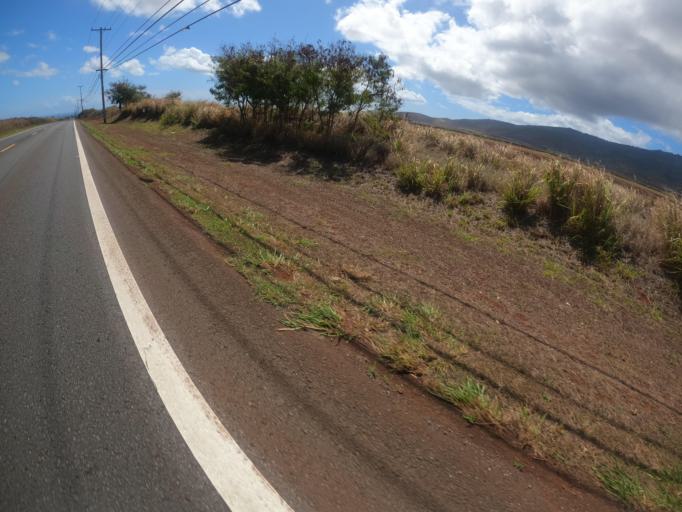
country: US
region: Hawaii
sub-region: Honolulu County
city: Village Park
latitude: 21.4115
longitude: -158.0449
